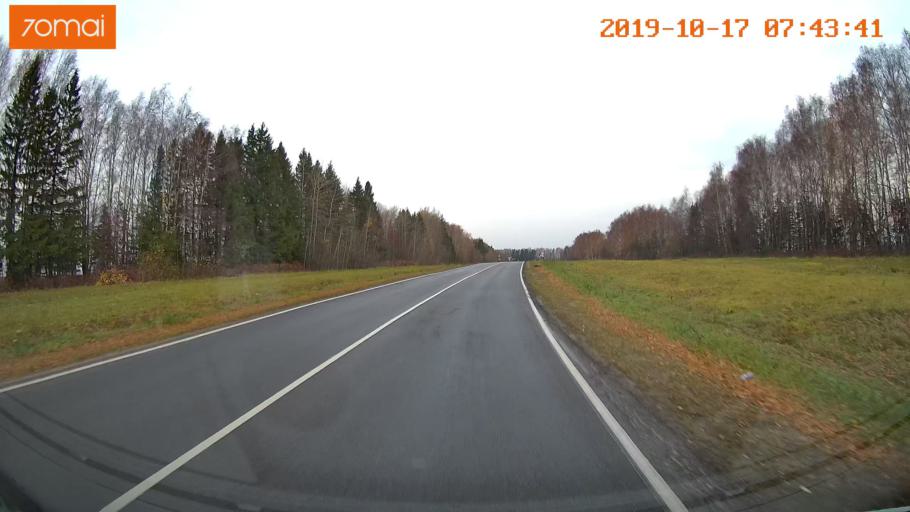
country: RU
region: Vladimir
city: Yur'yev-Pol'skiy
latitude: 56.4835
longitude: 39.7587
